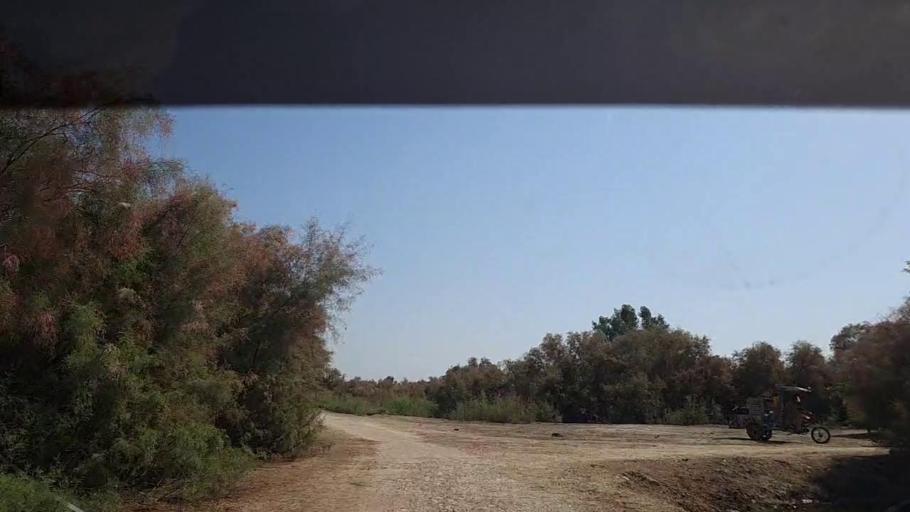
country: PK
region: Sindh
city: Ghauspur
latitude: 28.2073
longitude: 69.0775
